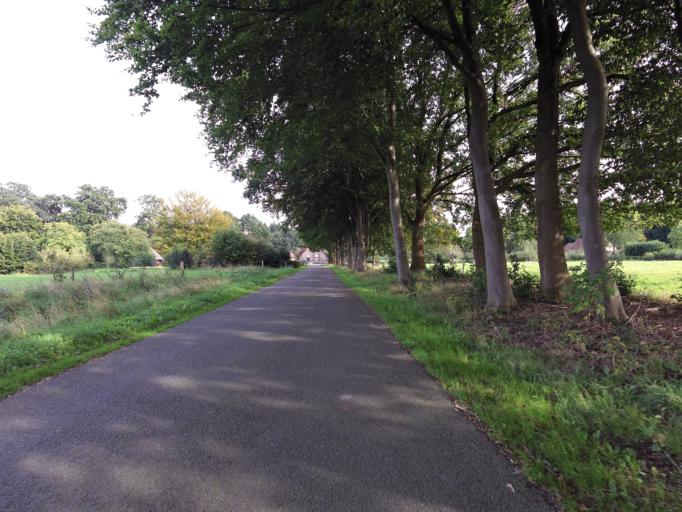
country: NL
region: Gelderland
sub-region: Gemeente Bronckhorst
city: Baak
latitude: 52.0198
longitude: 6.2099
